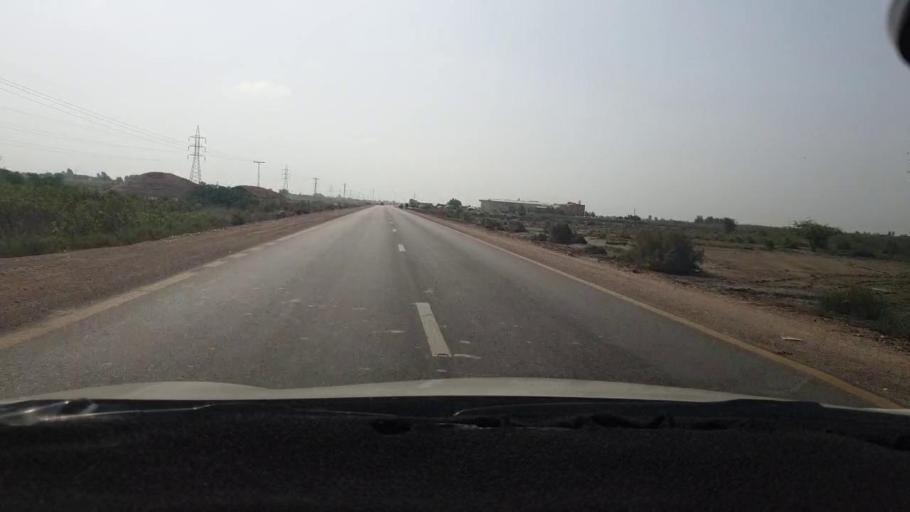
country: PK
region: Sindh
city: Jhol
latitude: 25.9026
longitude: 69.0207
